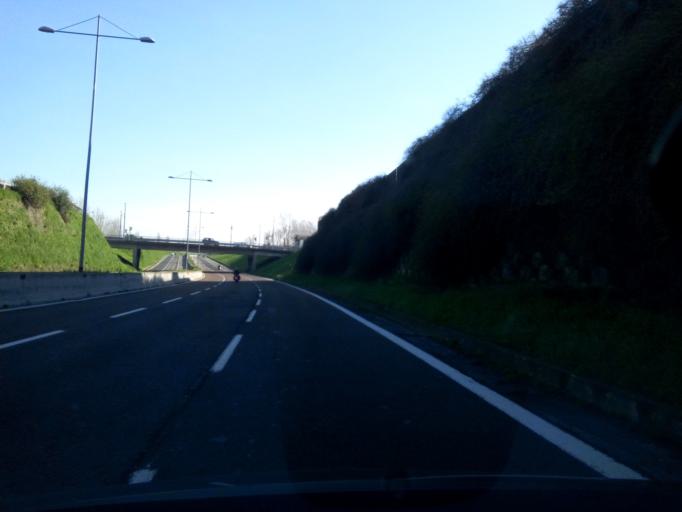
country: IT
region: Emilia-Romagna
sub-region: Provincia di Bologna
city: Casalecchio di Reno
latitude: 44.4935
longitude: 11.2943
